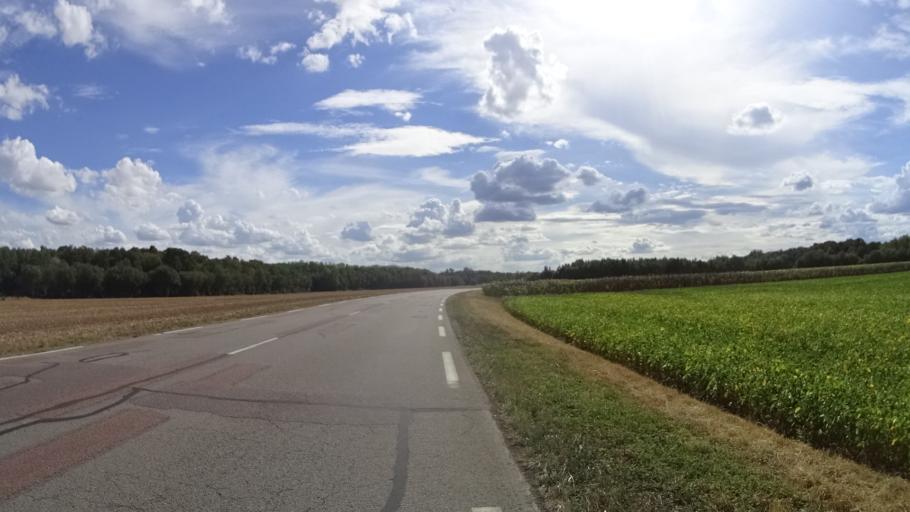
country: FR
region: Bourgogne
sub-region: Departement de la Cote-d'Or
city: Seurre
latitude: 47.0400
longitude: 5.1863
